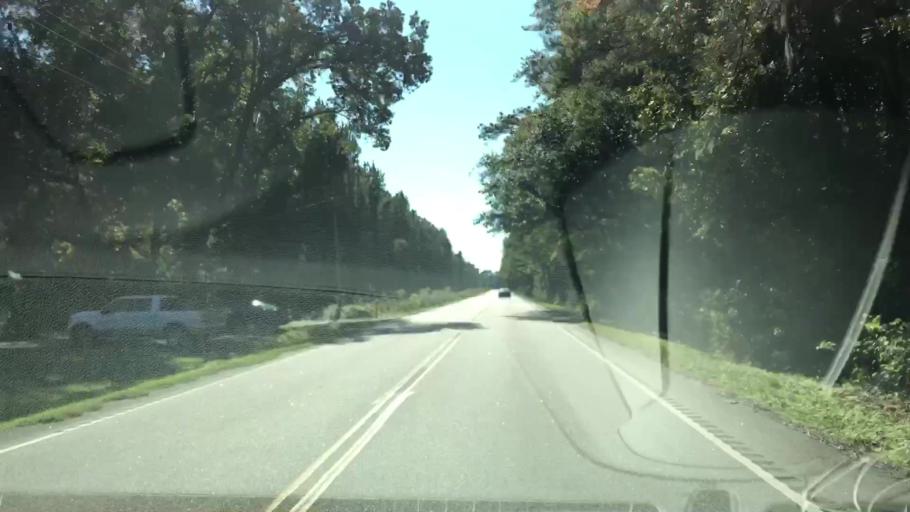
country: US
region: South Carolina
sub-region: Jasper County
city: Ridgeland
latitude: 32.5056
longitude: -80.8871
